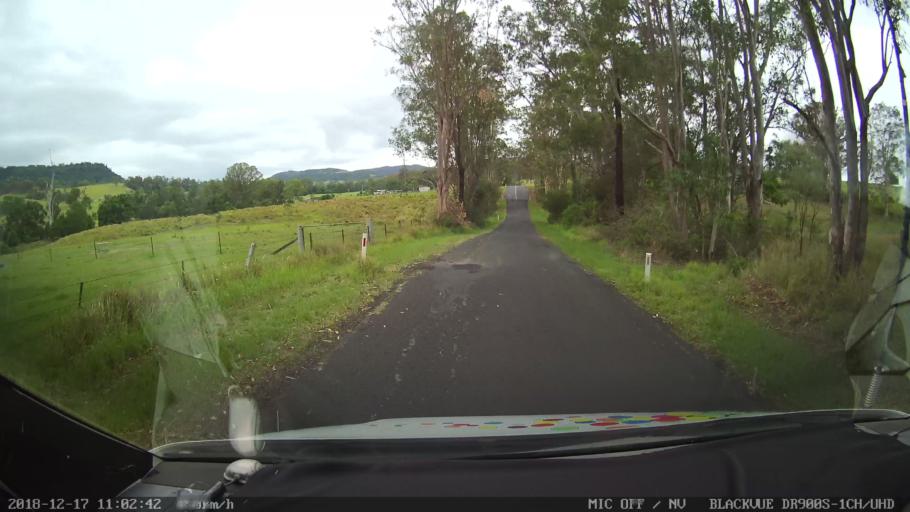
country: AU
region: New South Wales
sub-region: Richmond Valley
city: Casino
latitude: -28.8105
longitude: 152.6334
